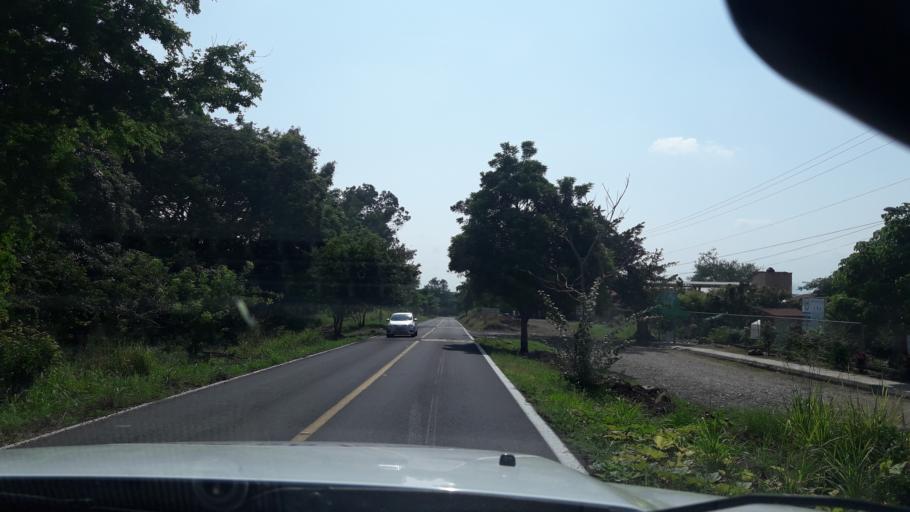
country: MX
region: Colima
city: Comala
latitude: 19.3343
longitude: -103.7474
